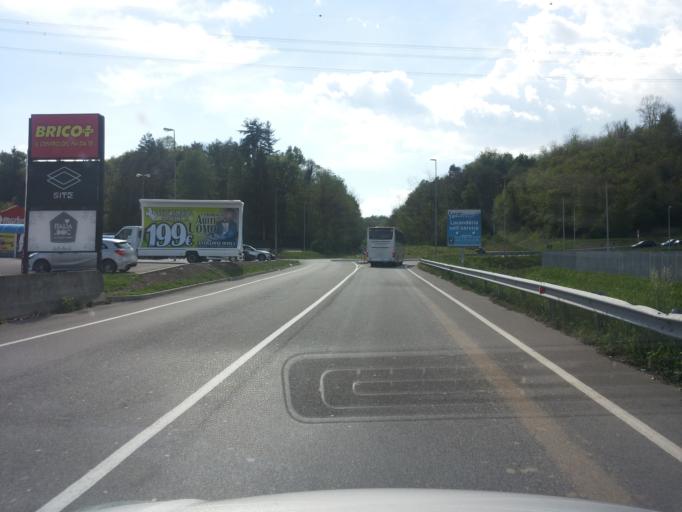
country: IT
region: Lombardy
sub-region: Provincia di Como
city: Rodero
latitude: 45.8372
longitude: 8.9067
